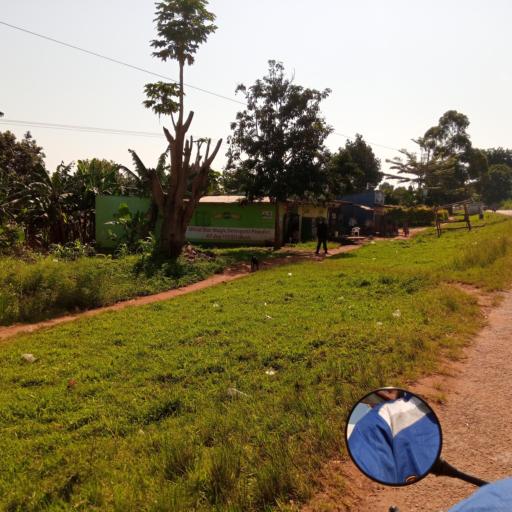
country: UG
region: Central Region
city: Masaka
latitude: -0.3779
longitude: 31.7111
